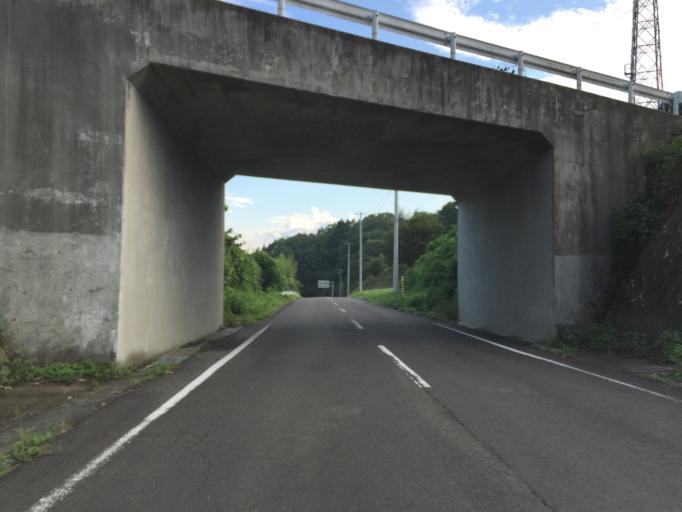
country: JP
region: Fukushima
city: Fukushima-shi
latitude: 37.6562
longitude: 140.5679
